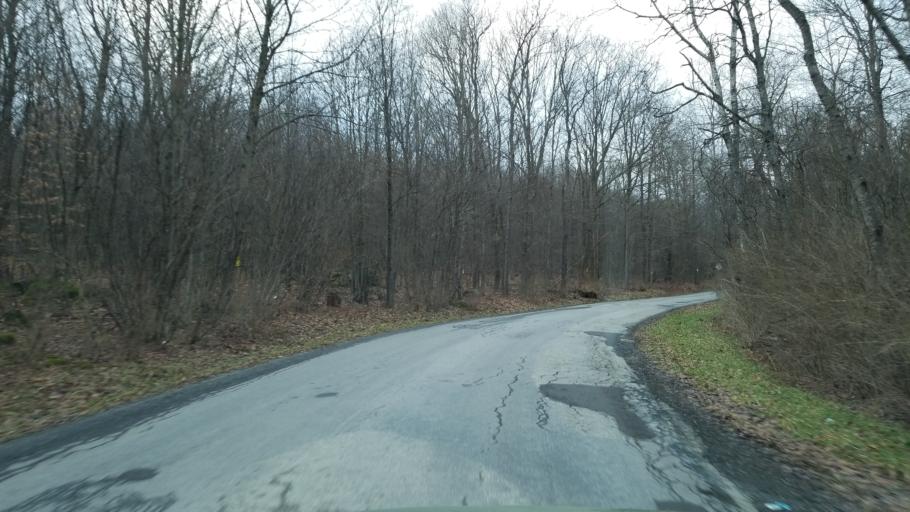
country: US
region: Pennsylvania
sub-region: Jefferson County
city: Falls Creek
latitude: 41.1730
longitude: -78.7886
